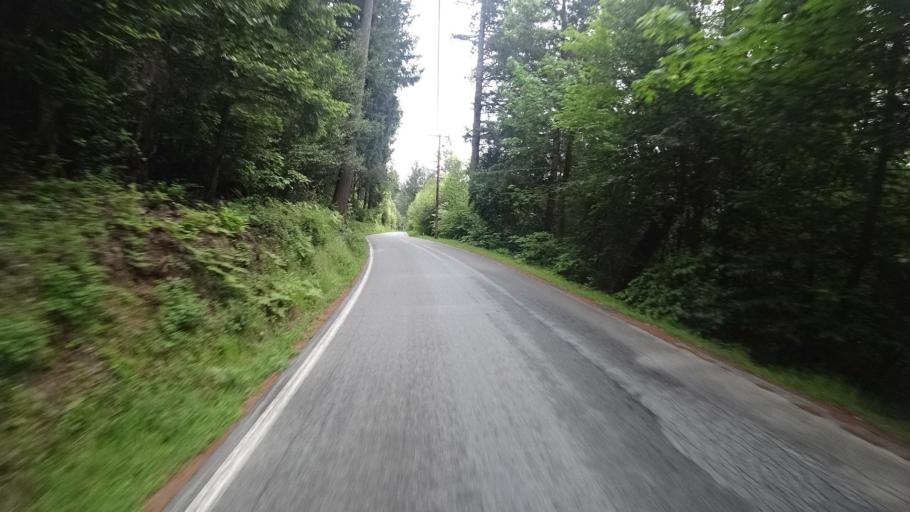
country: US
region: California
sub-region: Humboldt County
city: Willow Creek
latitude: 41.2009
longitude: -123.7490
